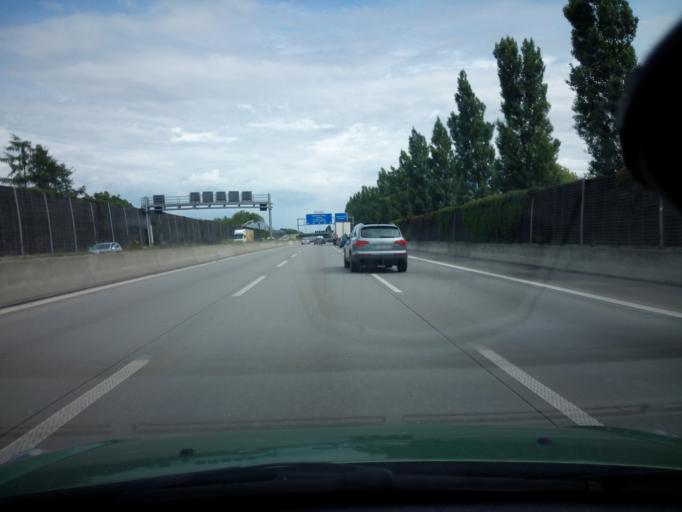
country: DE
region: Berlin
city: Buckow
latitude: 52.4459
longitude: 13.4725
